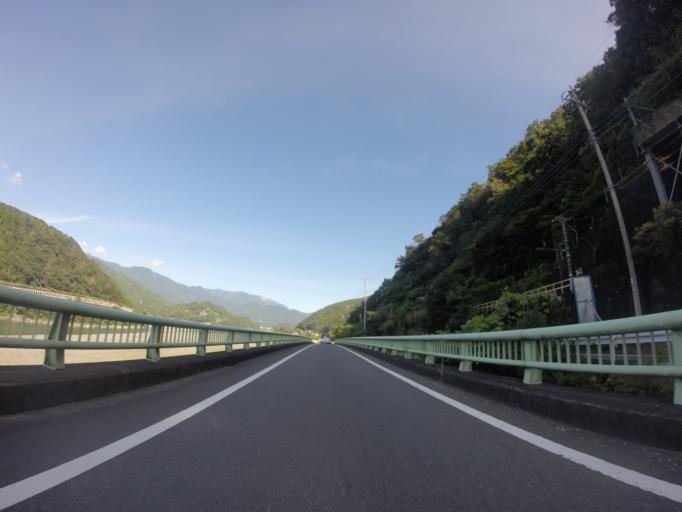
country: JP
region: Shizuoka
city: Fujinomiya
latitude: 35.2567
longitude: 138.4810
